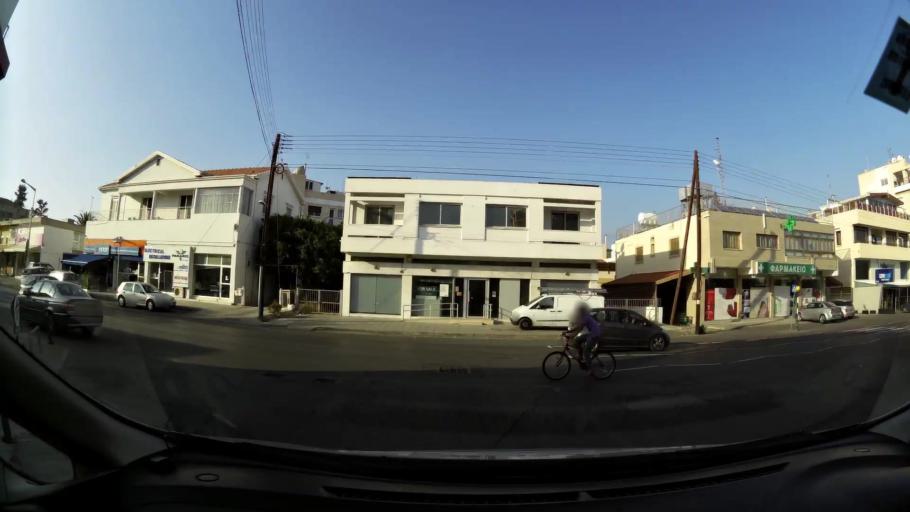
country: CY
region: Lefkosia
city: Nicosia
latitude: 35.1711
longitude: 33.3361
